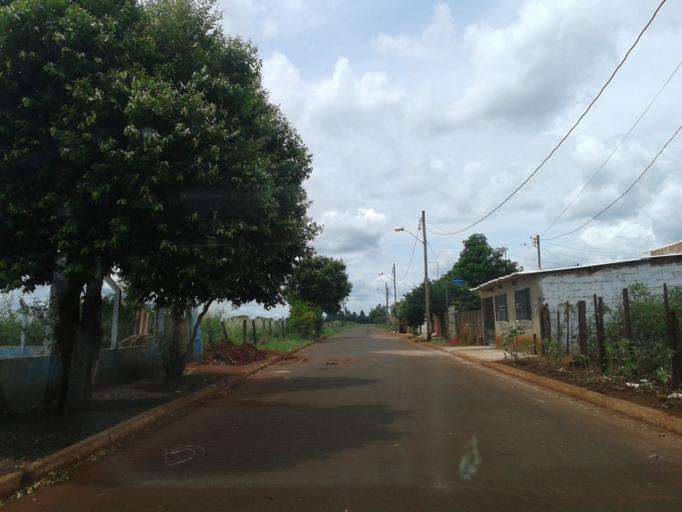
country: BR
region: Minas Gerais
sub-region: Centralina
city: Centralina
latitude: -18.5793
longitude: -49.2091
